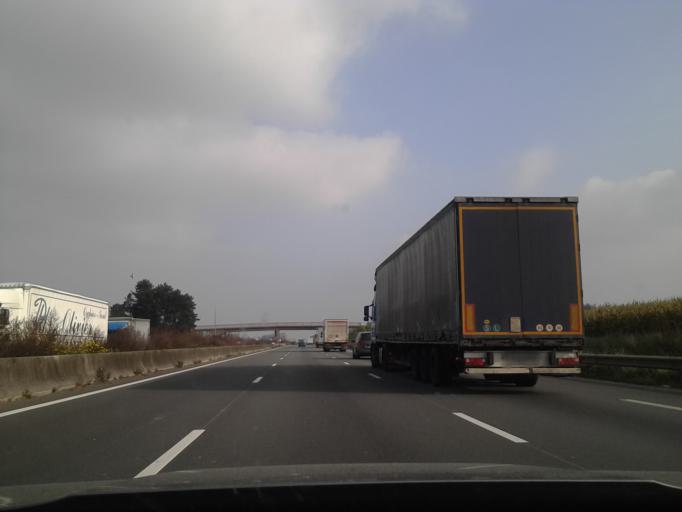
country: FR
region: Nord-Pas-de-Calais
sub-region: Departement du Nord
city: Vendeville
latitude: 50.5617
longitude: 3.0695
